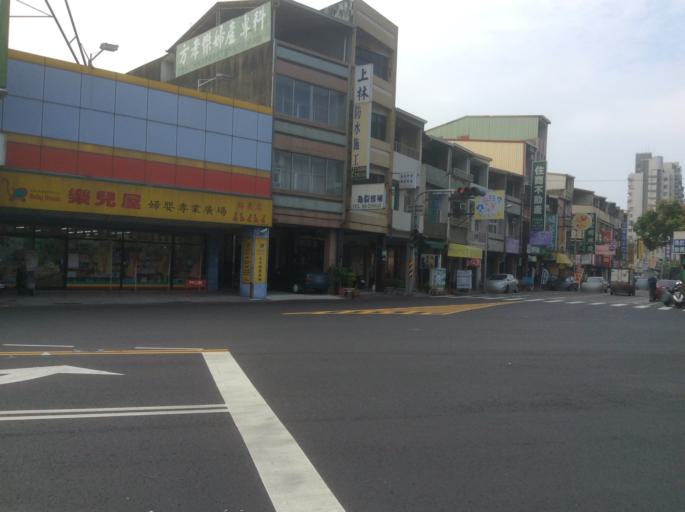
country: TW
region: Taiwan
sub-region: Tainan
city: Tainan
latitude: 22.9886
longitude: 120.2329
